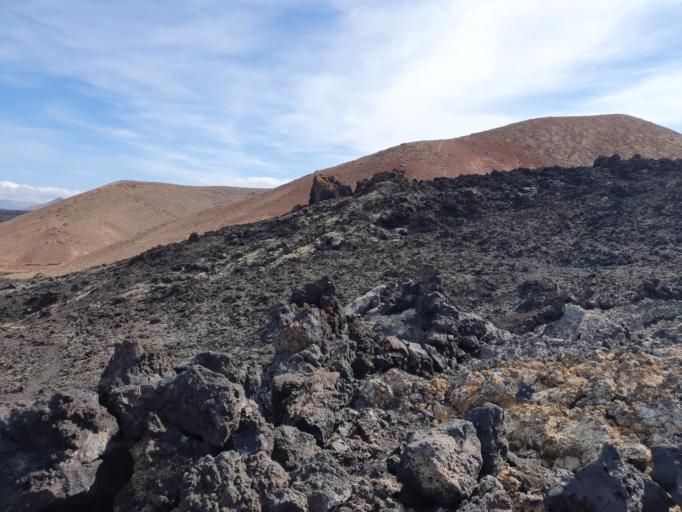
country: ES
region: Canary Islands
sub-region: Provincia de Las Palmas
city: Tinajo
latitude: 29.0425
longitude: -13.7221
